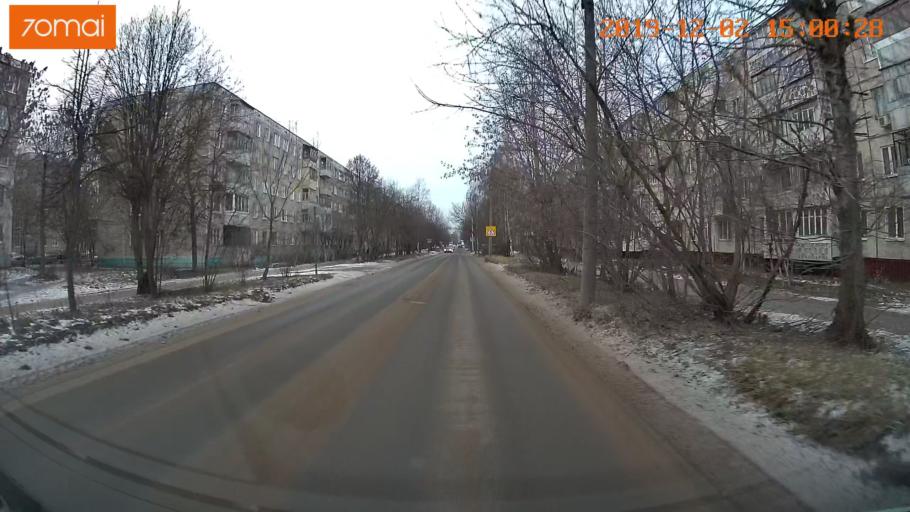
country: RU
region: Ivanovo
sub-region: Gorod Ivanovo
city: Ivanovo
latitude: 56.9704
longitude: 41.0038
